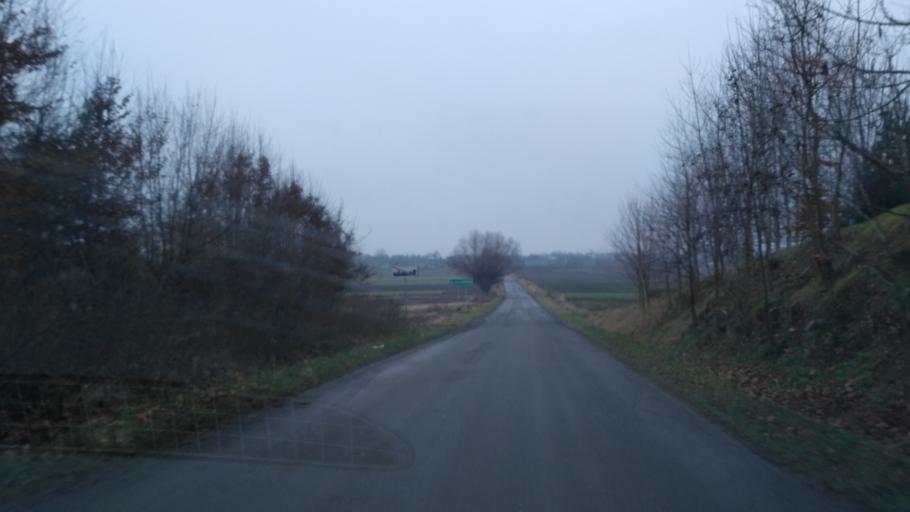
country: PL
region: Subcarpathian Voivodeship
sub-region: Powiat przeworski
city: Zarzecze
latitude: 49.9711
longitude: 22.5661
